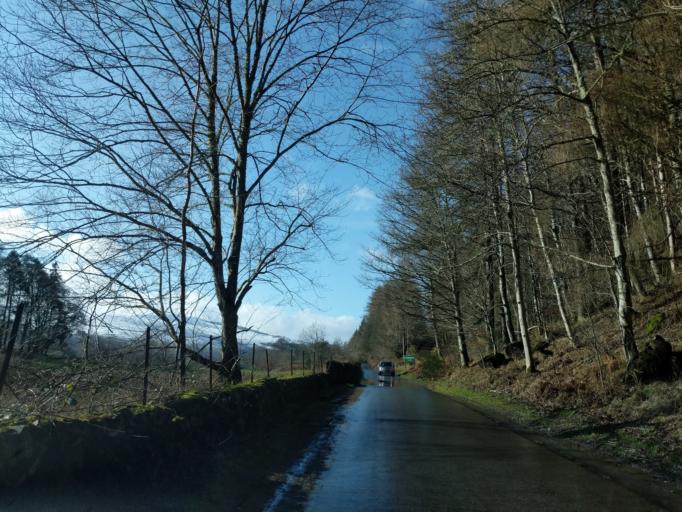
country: GB
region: Scotland
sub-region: Perth and Kinross
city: Aberfeldy
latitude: 56.5913
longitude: -3.9980
